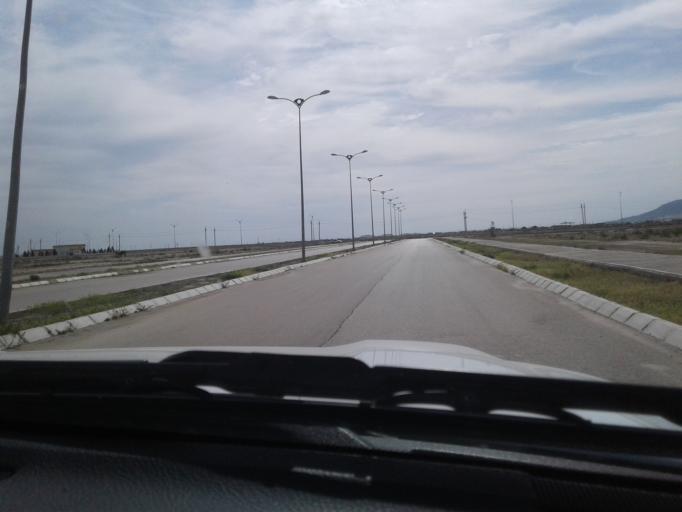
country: TM
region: Balkan
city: Gazanjyk
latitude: 39.2662
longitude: 55.4962
